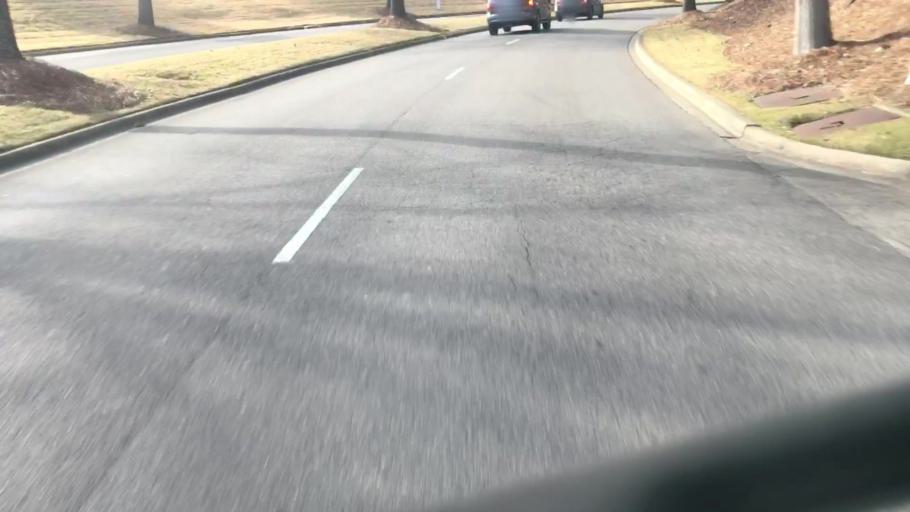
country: US
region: Alabama
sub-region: Jefferson County
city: Cahaba Heights
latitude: 33.4807
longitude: -86.7048
